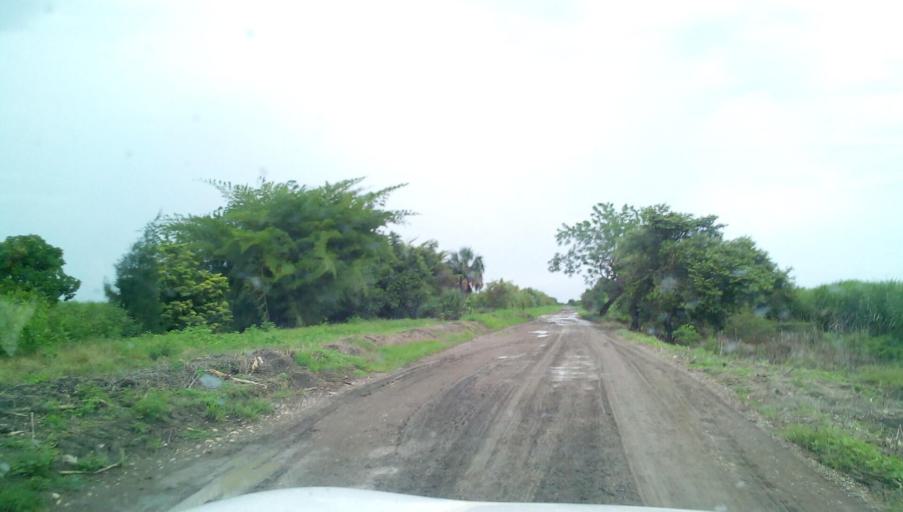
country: MX
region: Veracruz
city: Panuco
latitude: 21.8197
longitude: -98.1109
